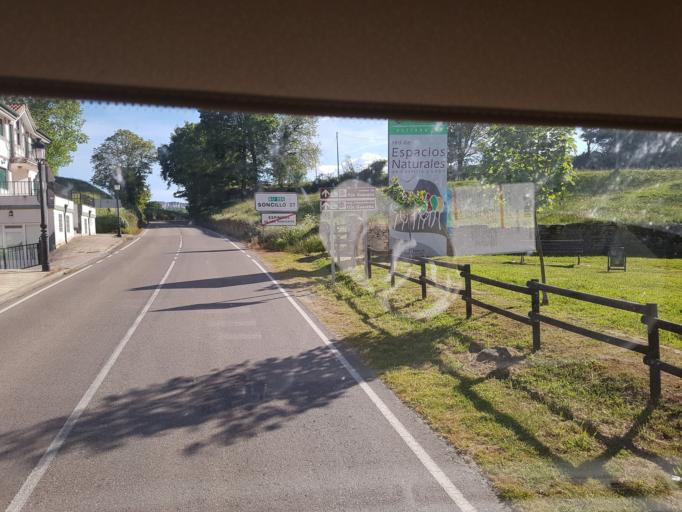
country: ES
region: Castille and Leon
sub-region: Provincia de Burgos
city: Espinosa de los Monteros
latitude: 43.0748
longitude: -3.5570
